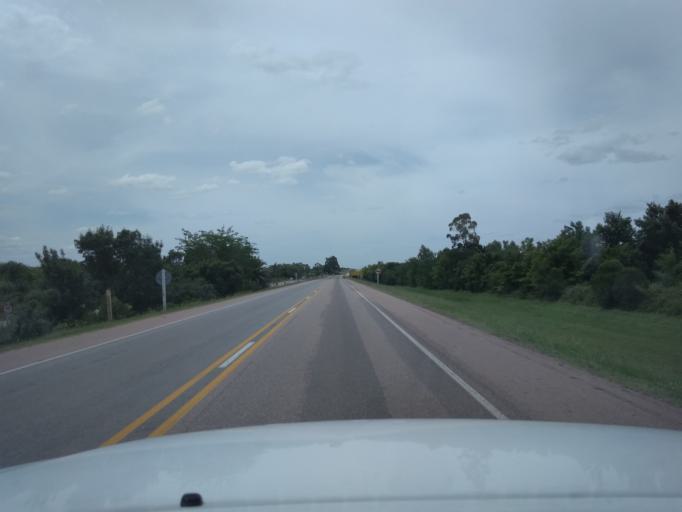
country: UY
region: Canelones
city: Canelones
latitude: -34.5013
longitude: -56.2817
